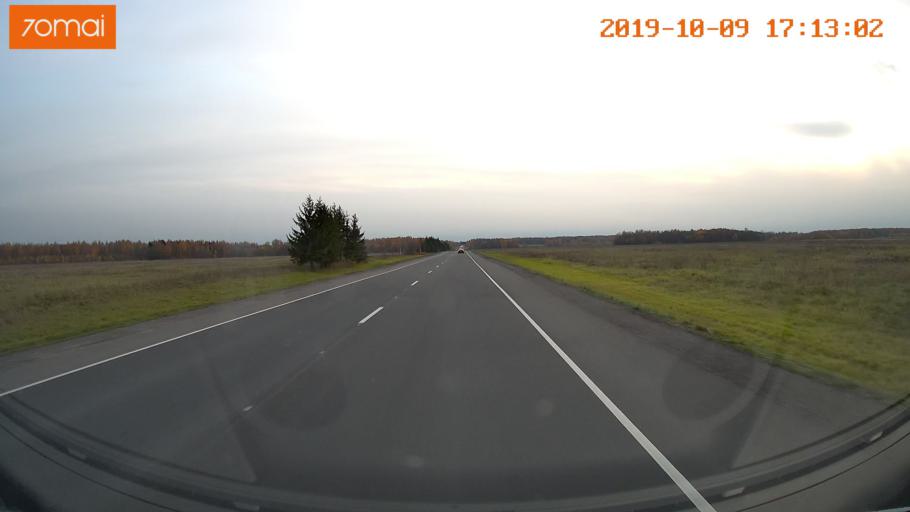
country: RU
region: Ivanovo
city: Privolzhsk
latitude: 57.3204
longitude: 41.2312
